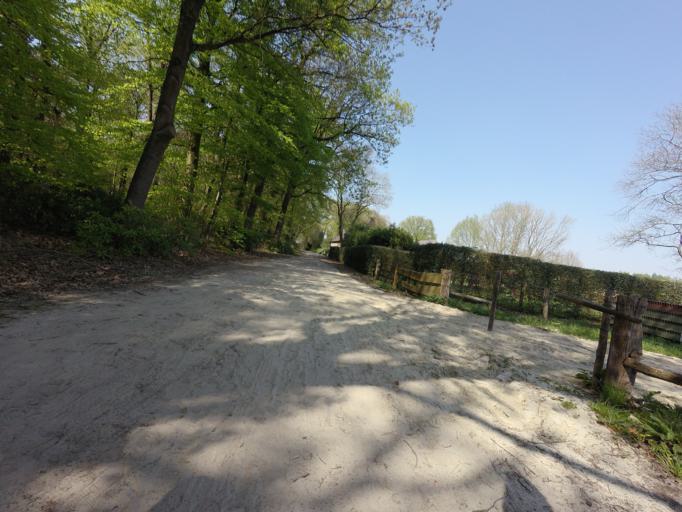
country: NL
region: North Brabant
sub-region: Gemeente Goirle
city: Goirle
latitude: 51.5034
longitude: 5.0168
